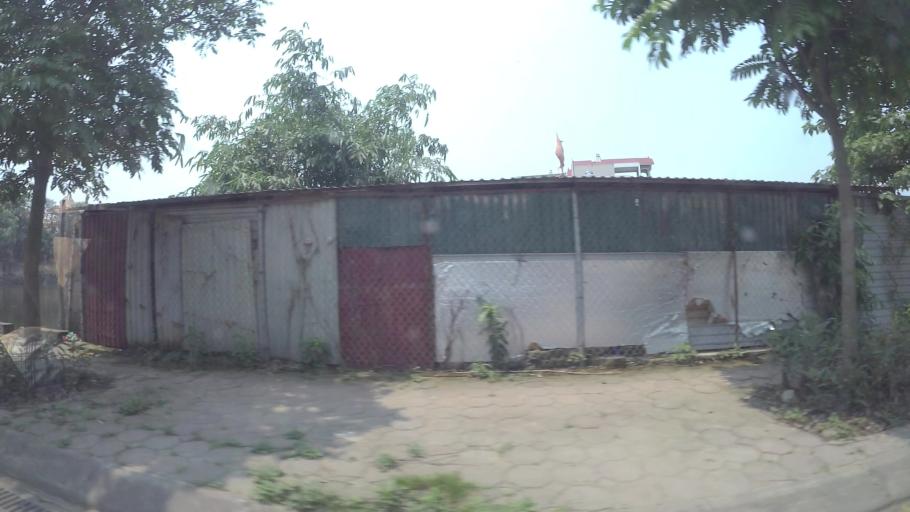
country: VN
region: Ha Noi
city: Van Dien
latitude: 20.9502
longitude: 105.8325
